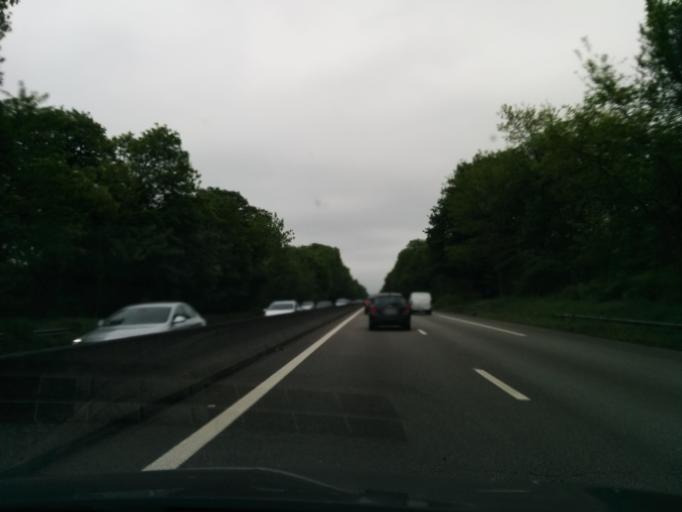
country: FR
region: Ile-de-France
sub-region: Departement des Yvelines
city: Noisy-le-Roi
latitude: 48.8607
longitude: 2.0471
